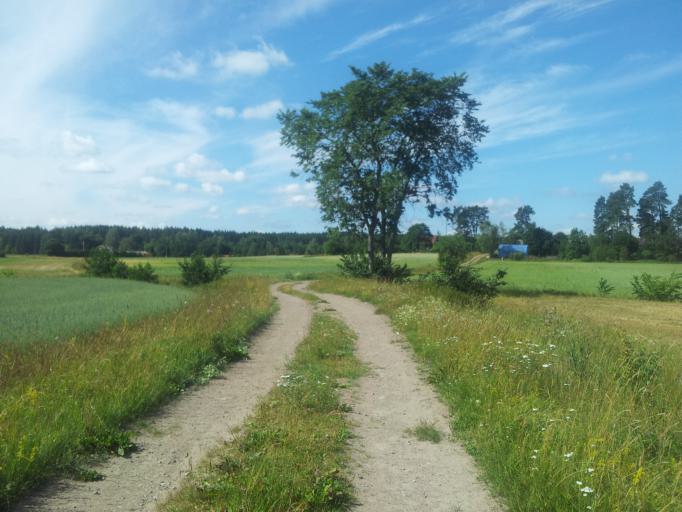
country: SE
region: Stockholm
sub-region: Norrtalje Kommun
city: Nykvarn
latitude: 59.8913
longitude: 18.2335
